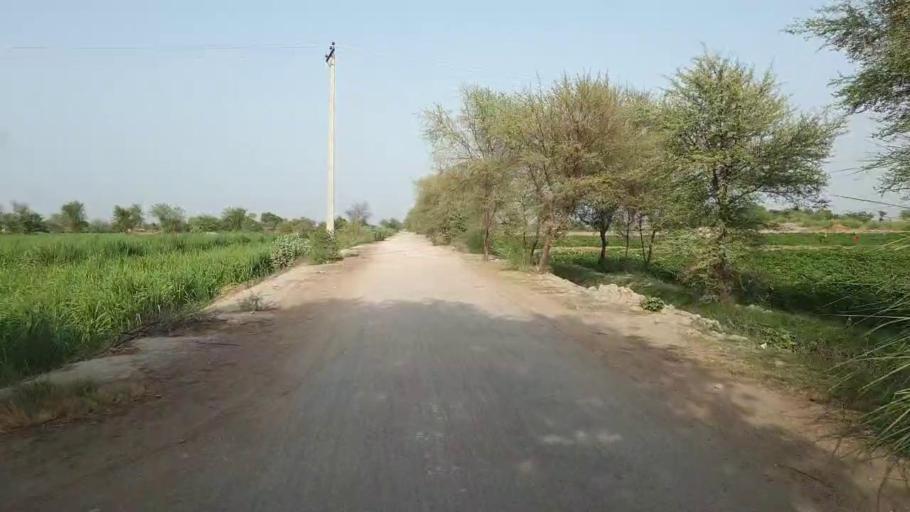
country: PK
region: Sindh
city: Daur
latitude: 26.3432
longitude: 68.2647
